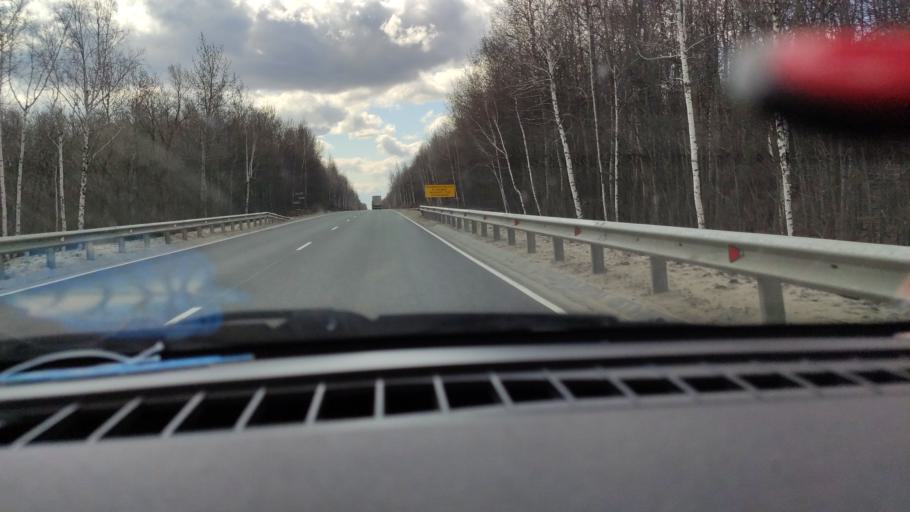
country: RU
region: Saratov
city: Khvalynsk
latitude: 52.4372
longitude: 48.0092
